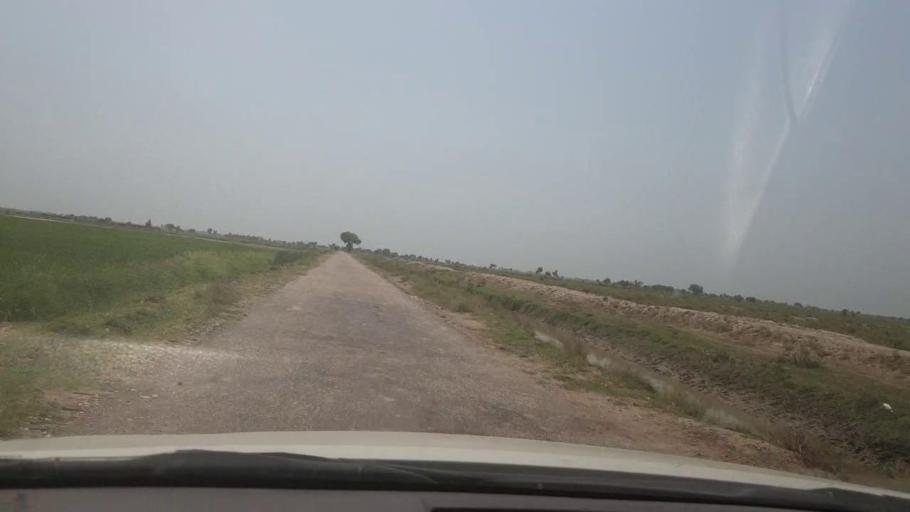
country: PK
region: Sindh
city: Shikarpur
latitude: 28.0457
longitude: 68.5727
